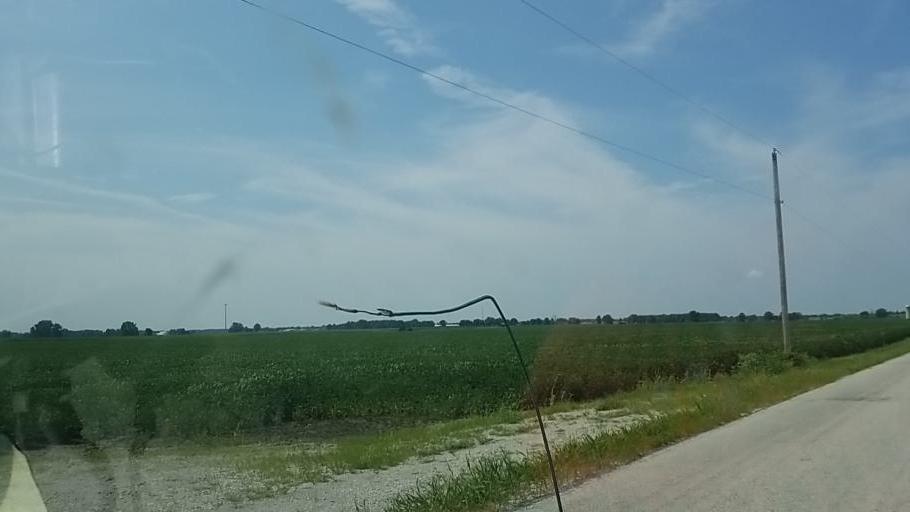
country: US
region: Ohio
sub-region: Marion County
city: Marion
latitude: 40.5973
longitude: -83.0462
